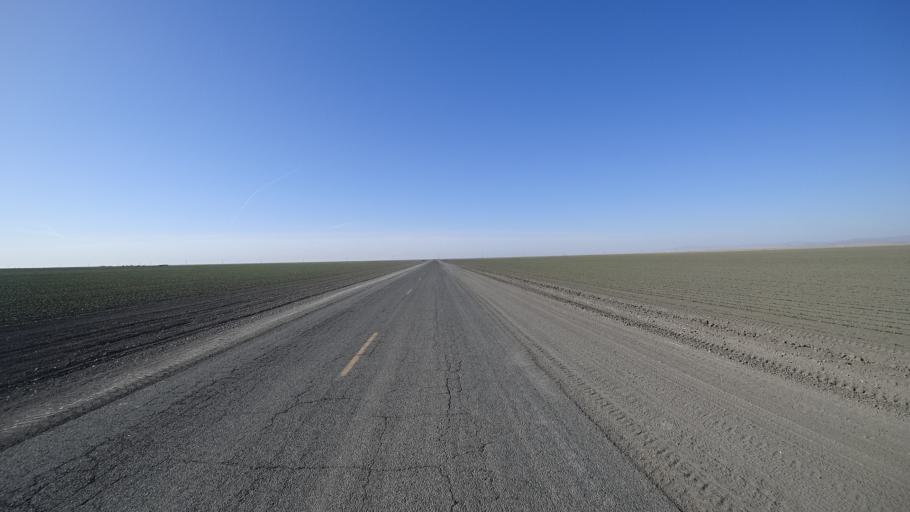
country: US
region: California
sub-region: Kings County
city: Stratford
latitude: 36.0861
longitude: -119.7979
